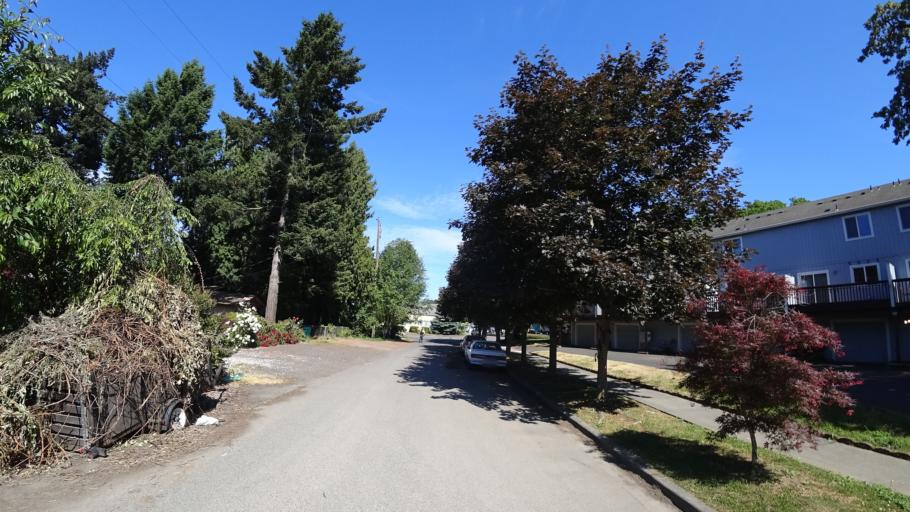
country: US
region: Washington
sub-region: Clark County
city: Vancouver
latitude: 45.5938
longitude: -122.7312
